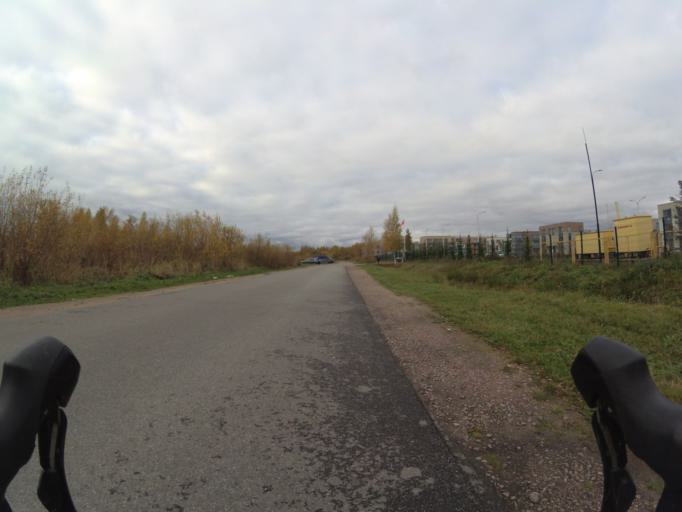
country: RU
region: St.-Petersburg
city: Lakhtinskiy
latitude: 60.0033
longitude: 30.1531
